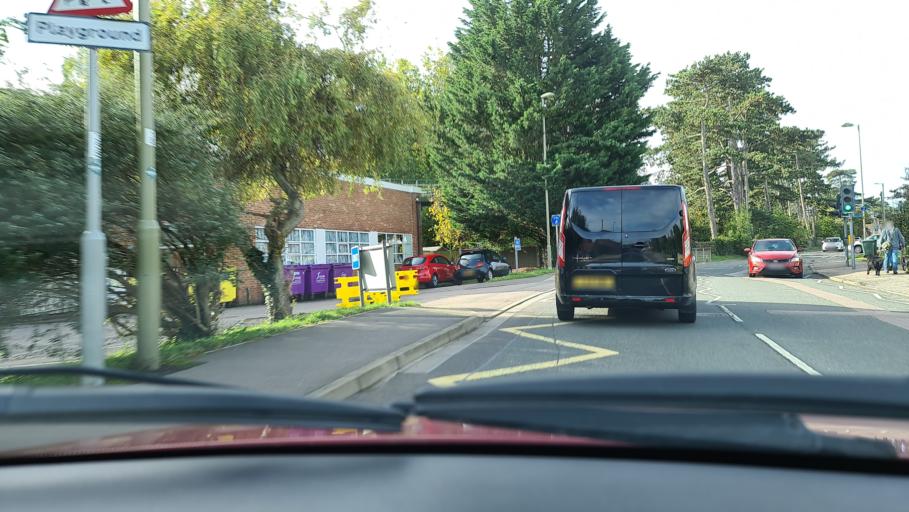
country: GB
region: England
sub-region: Oxfordshire
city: Bicester
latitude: 51.8979
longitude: -1.1432
